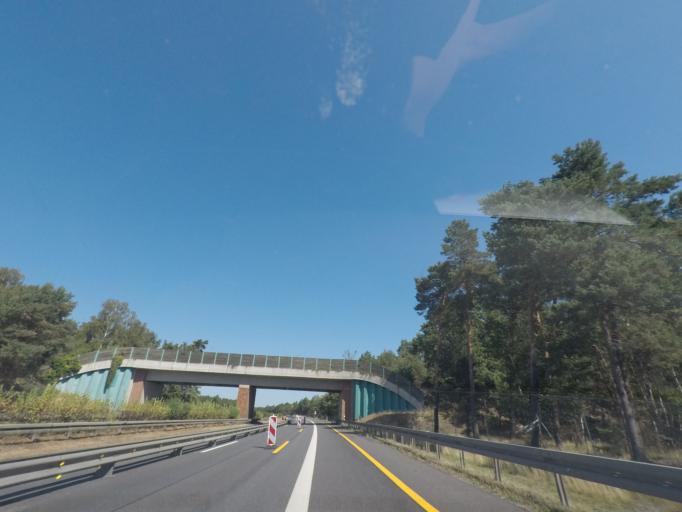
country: DE
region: Brandenburg
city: Grossraschen
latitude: 51.6041
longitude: 13.9541
